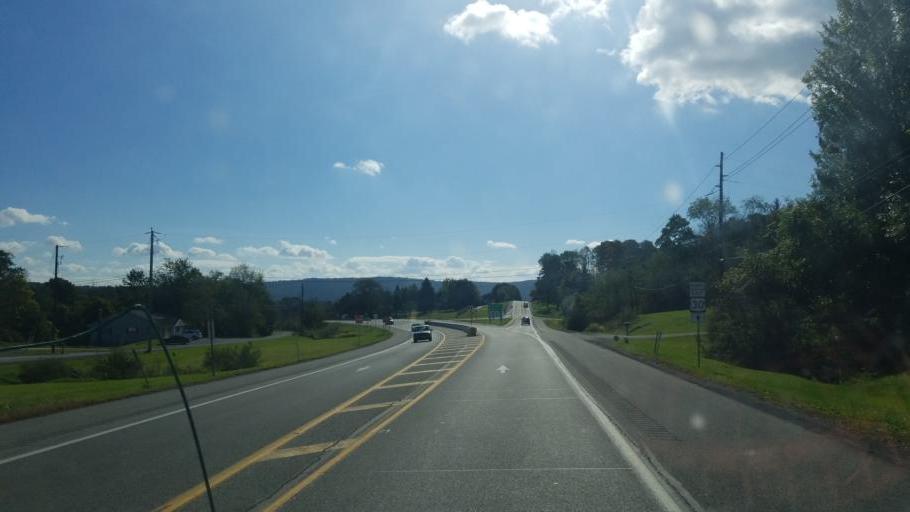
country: US
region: Pennsylvania
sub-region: Bedford County
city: Bedford
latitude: 40.0381
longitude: -78.5244
